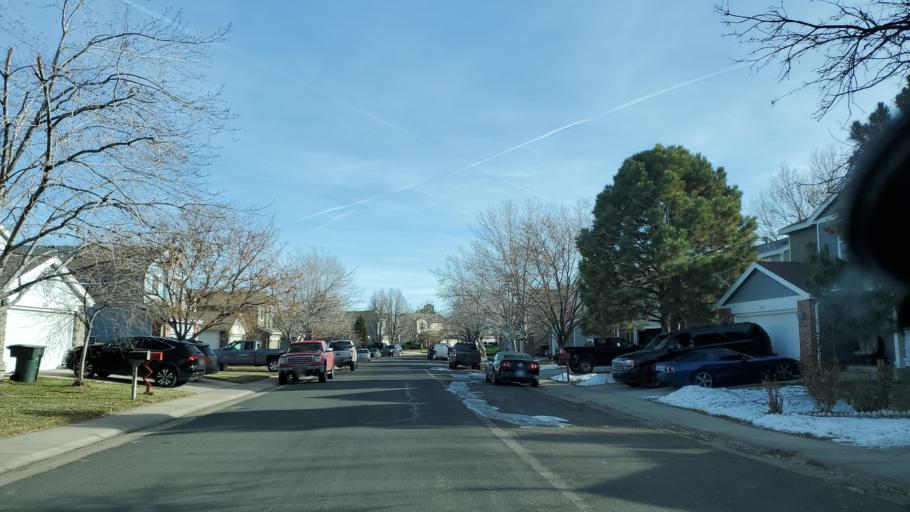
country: US
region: Colorado
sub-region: Adams County
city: Northglenn
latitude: 39.9115
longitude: -104.9534
